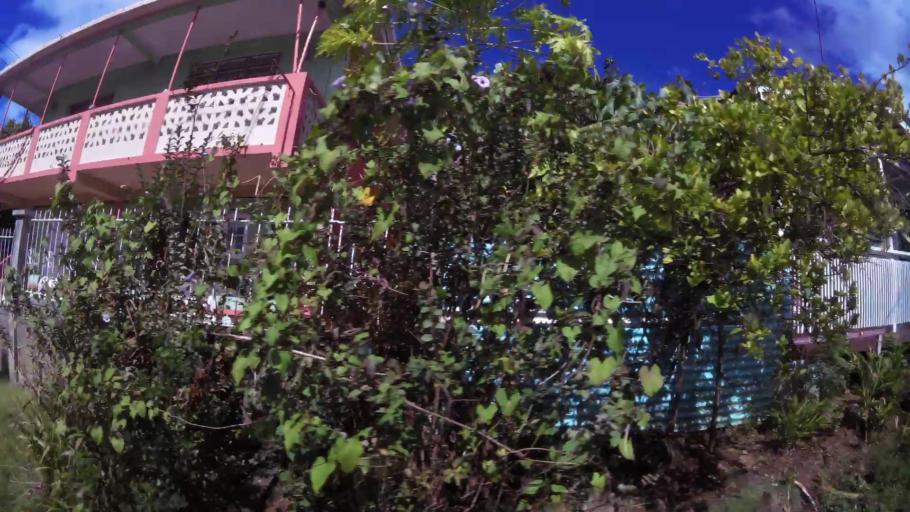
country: DM
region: Saint John
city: Portsmouth
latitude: 15.5782
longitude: -61.4536
